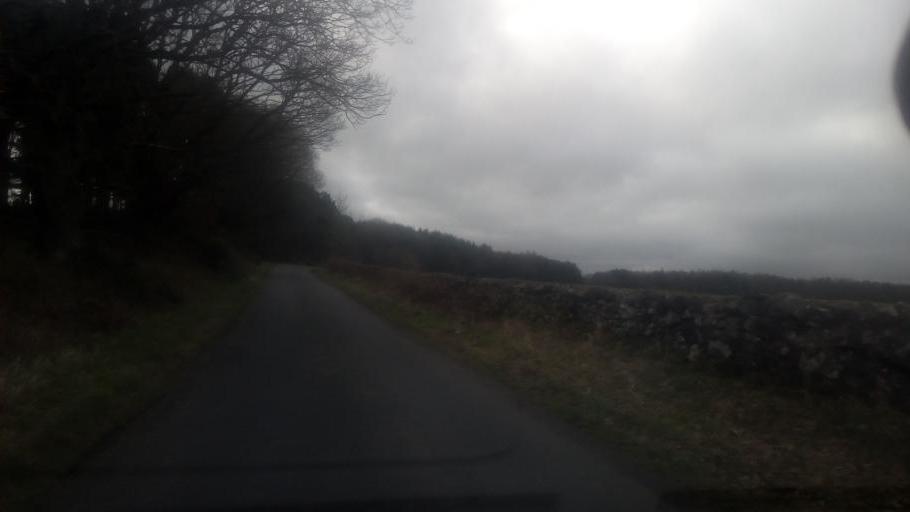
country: GB
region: Scotland
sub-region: The Scottish Borders
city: Kelso
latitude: 55.5484
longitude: -2.4893
